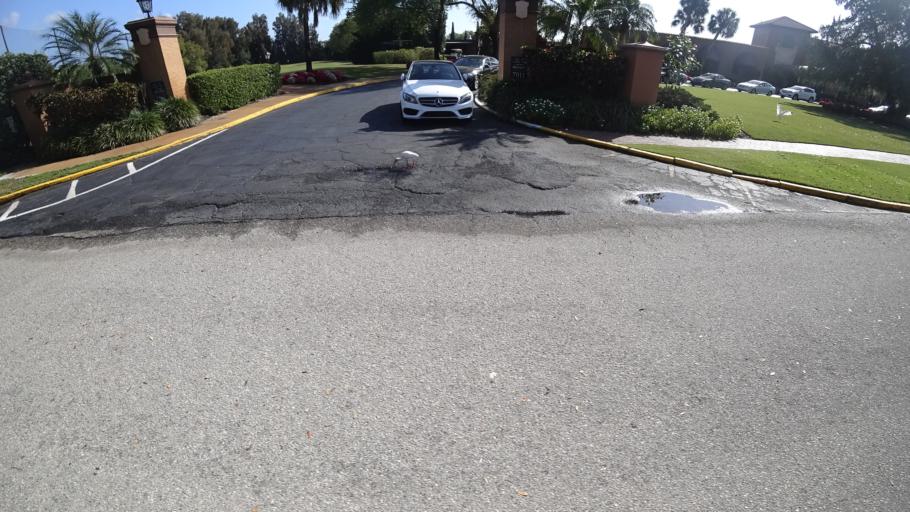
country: US
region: Florida
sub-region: Manatee County
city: Whitfield
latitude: 27.4158
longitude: -82.5681
